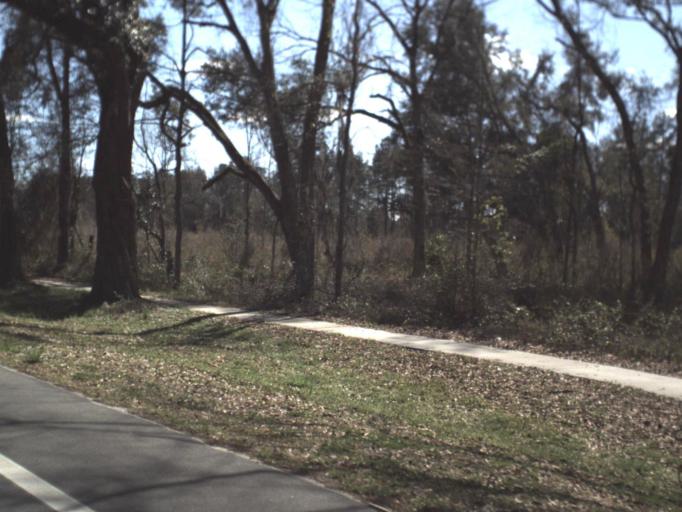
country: US
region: Florida
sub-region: Gadsden County
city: Gretna
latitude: 30.6116
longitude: -84.6598
